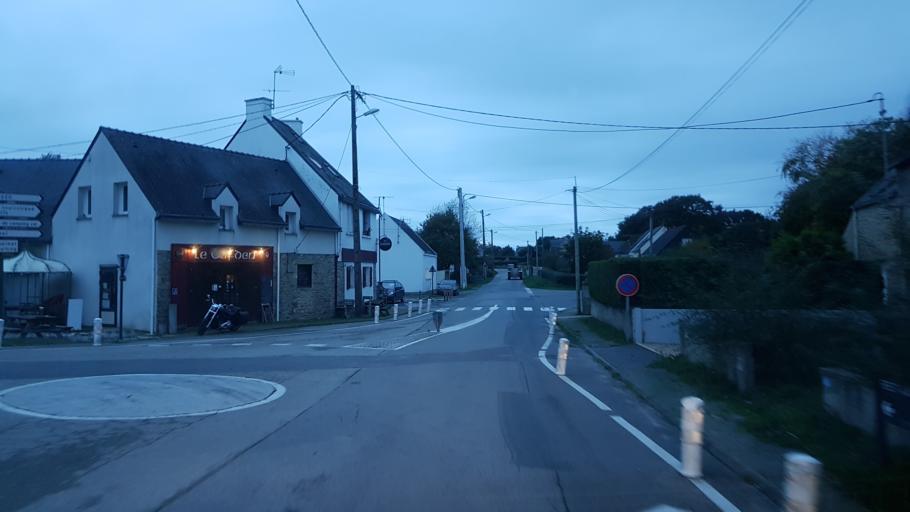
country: FR
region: Brittany
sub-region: Departement du Morbihan
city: Sarzeau
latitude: 47.5420
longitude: -2.8117
